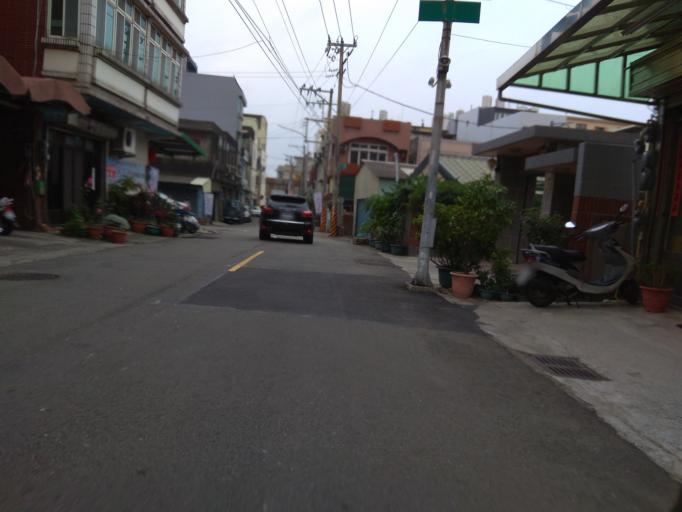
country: TW
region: Taiwan
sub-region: Hsinchu
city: Hsinchu
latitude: 24.7933
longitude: 120.9227
